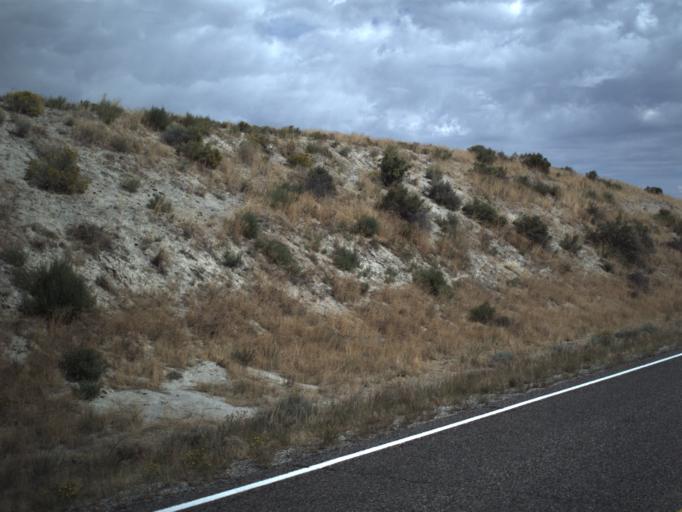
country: US
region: Utah
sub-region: Tooele County
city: Wendover
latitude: 41.4043
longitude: -113.9428
